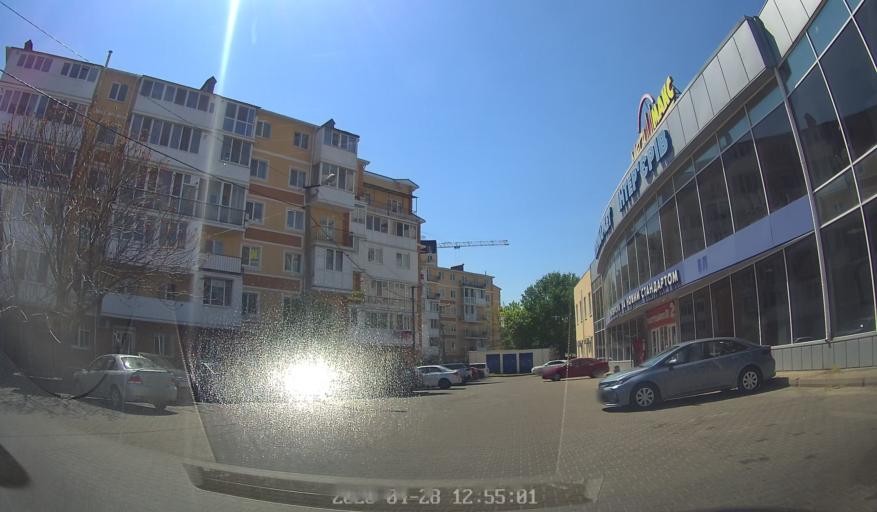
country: NE
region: Zinder
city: Mirriah
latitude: 13.9253
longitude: 9.2177
